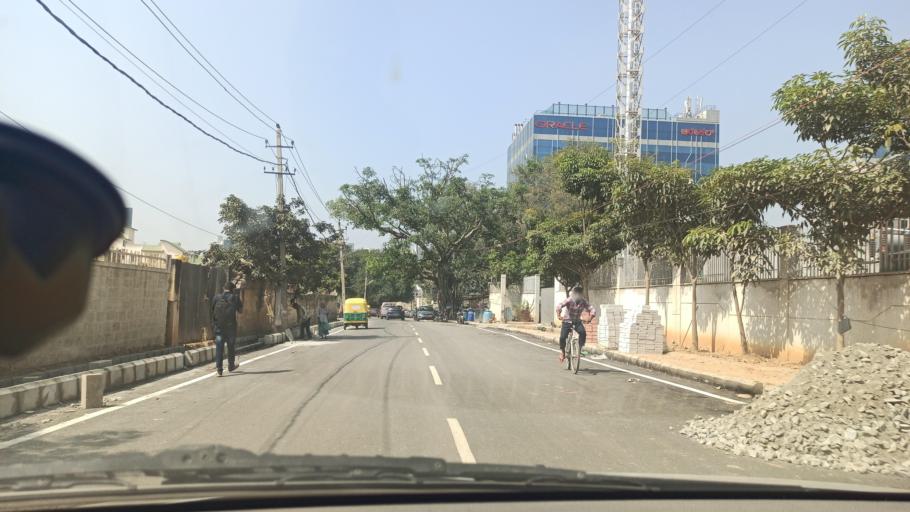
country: IN
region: Karnataka
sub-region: Bangalore Urban
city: Bangalore
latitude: 12.9397
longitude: 77.6941
